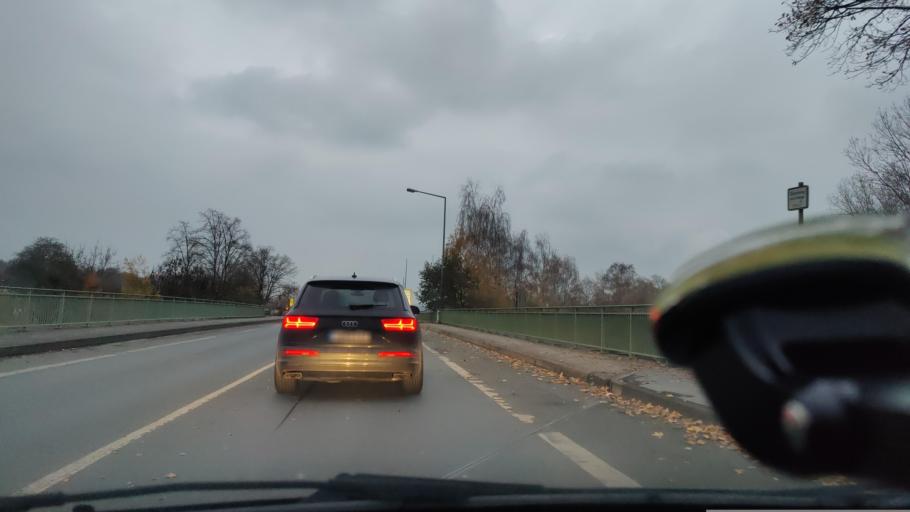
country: DE
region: North Rhine-Westphalia
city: Lunen
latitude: 51.6088
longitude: 7.5028
